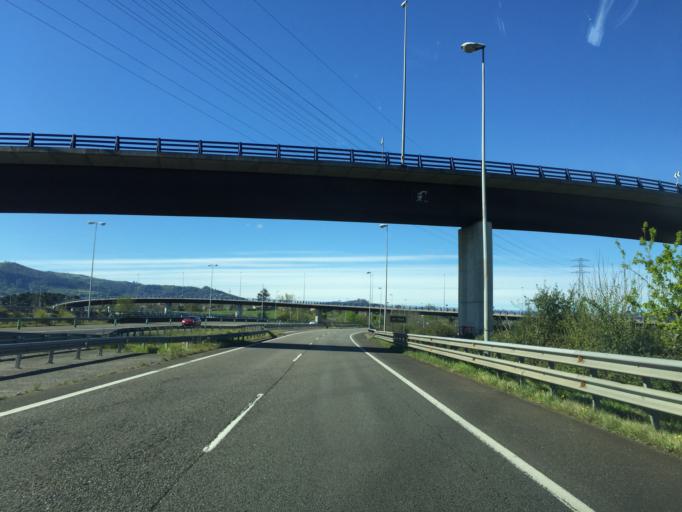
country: ES
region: Asturias
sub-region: Province of Asturias
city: Gijon
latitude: 43.5178
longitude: -5.6552
